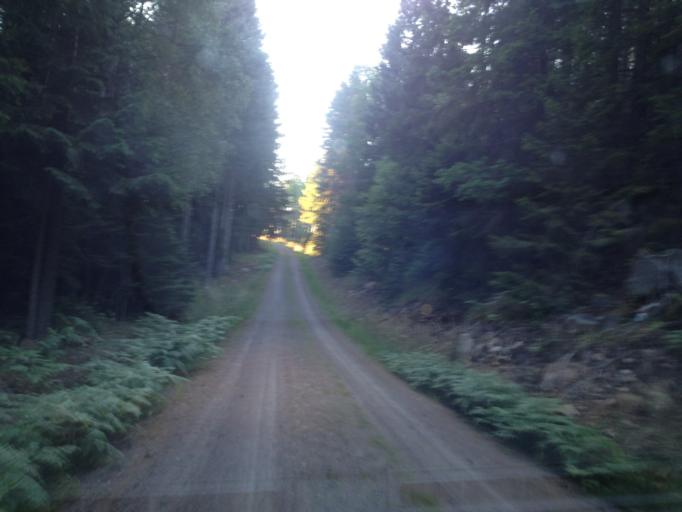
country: SE
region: Kalmar
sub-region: Vasterviks Kommun
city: Overum
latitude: 57.9983
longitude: 16.1347
